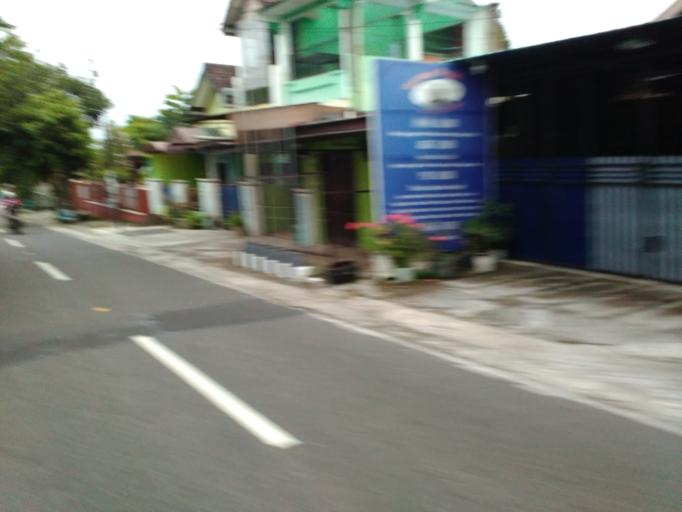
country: ID
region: Central Java
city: Boyolali
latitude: -7.5357
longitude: 110.6058
